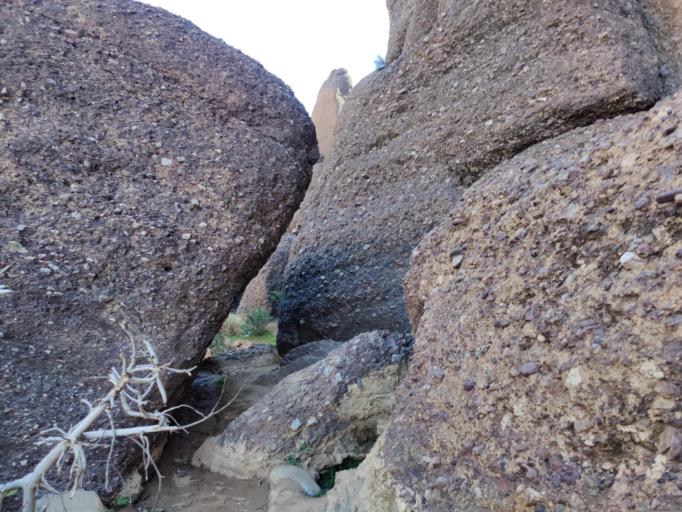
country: MA
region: Souss-Massa-Draa
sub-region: Taroudannt
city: Taliouine
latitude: 30.5548
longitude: -7.5924
